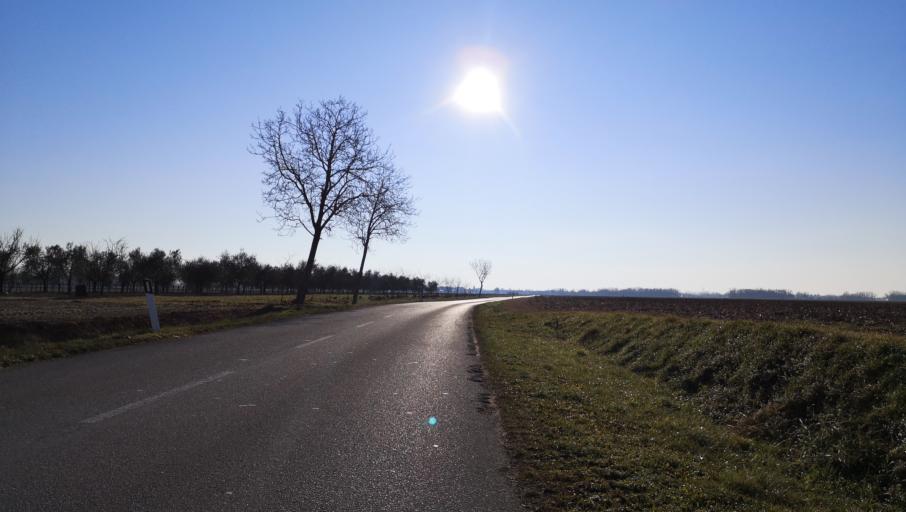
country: IT
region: Friuli Venezia Giulia
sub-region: Provincia di Udine
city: Santa Maria la Longa
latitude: 45.9489
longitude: 13.2724
